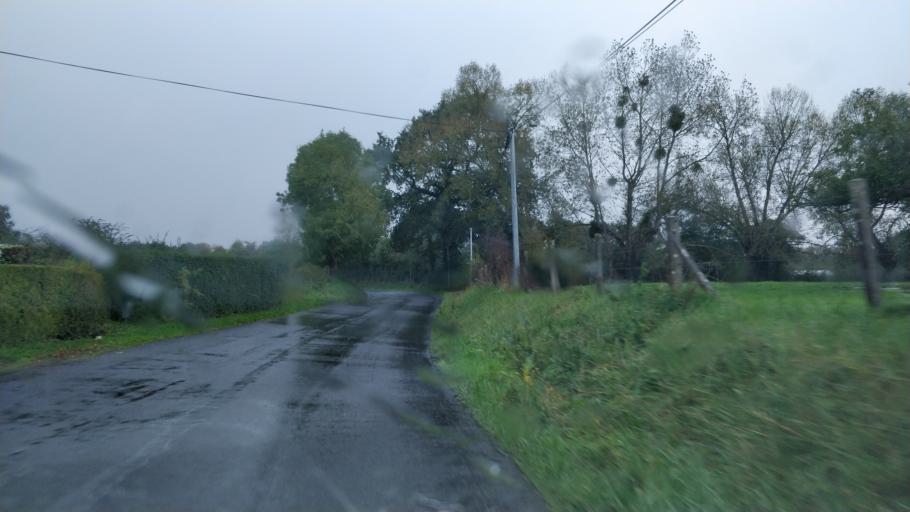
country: FR
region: Lower Normandy
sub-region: Departement de la Manche
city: Brehal
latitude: 48.9019
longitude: -1.5349
